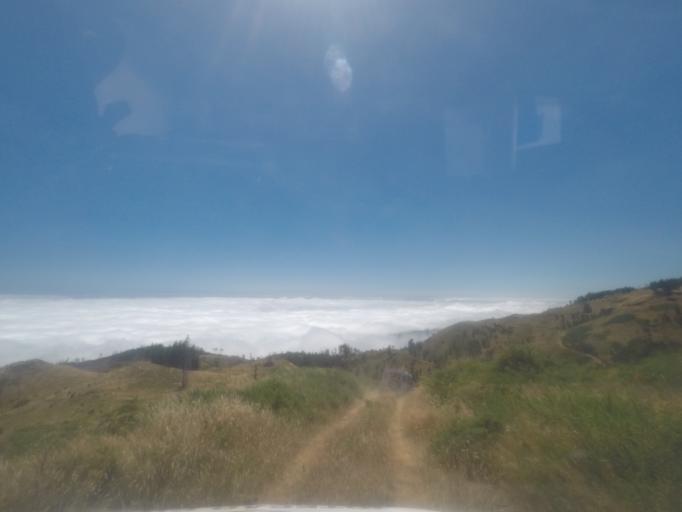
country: PT
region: Madeira
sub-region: Funchal
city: Nossa Senhora do Monte
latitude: 32.7060
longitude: -16.8974
